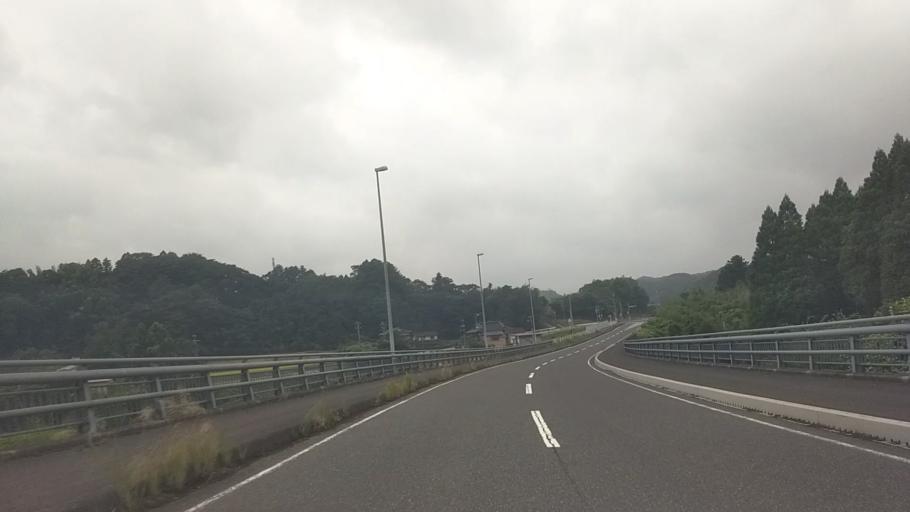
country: JP
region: Chiba
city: Kimitsu
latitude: 35.2594
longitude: 140.0477
